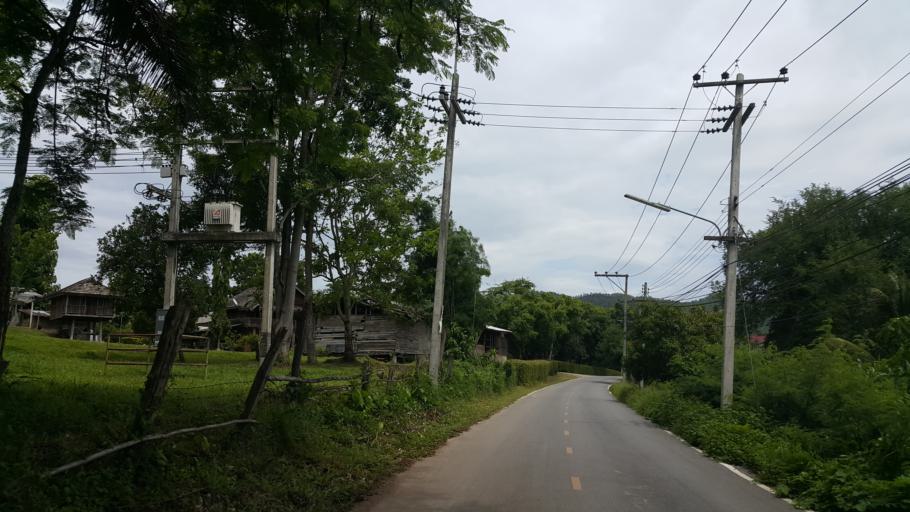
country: TH
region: Lampang
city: Mueang Pan
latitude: 18.7791
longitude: 99.5240
